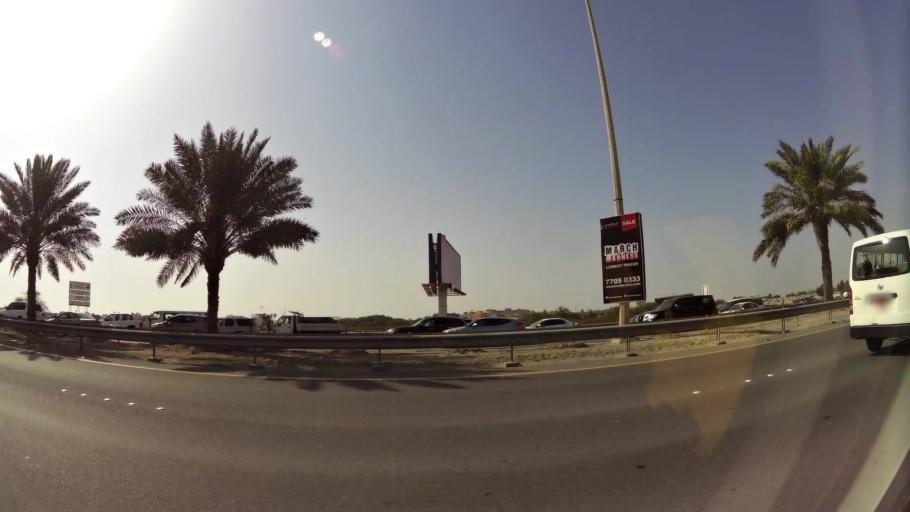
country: BH
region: Manama
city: Jidd Hafs
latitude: 26.2092
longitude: 50.5176
